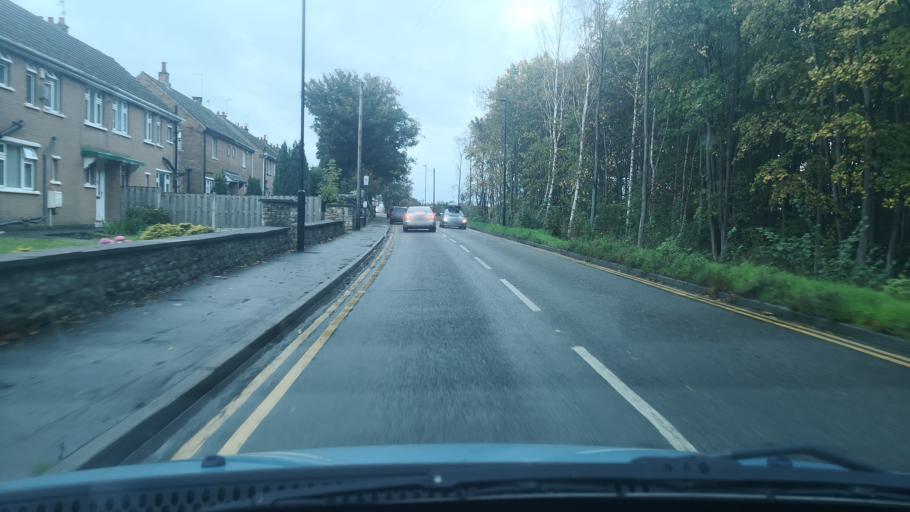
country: GB
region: England
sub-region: Doncaster
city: Campsall
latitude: 53.6222
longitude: -1.1722
